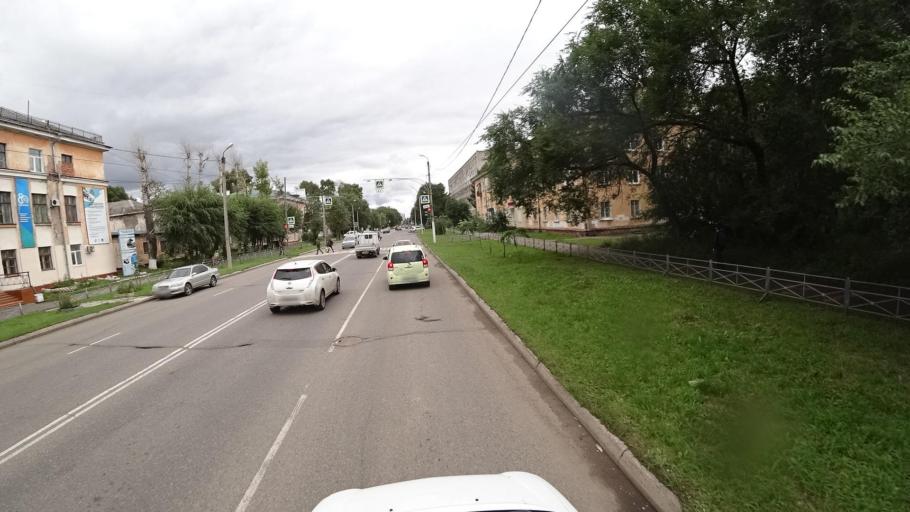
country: RU
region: Khabarovsk Krai
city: Komsomolsk-on-Amur
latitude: 50.5503
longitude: 137.0276
